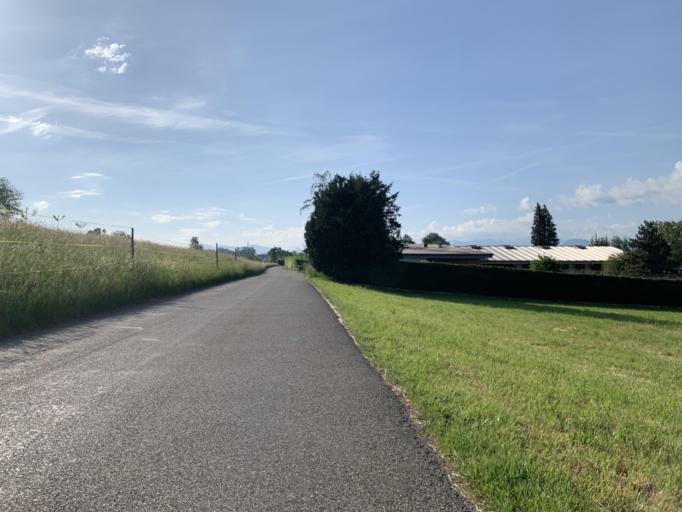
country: CH
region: Zurich
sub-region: Bezirk Hinwil
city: Gossau
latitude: 47.3109
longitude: 8.7495
